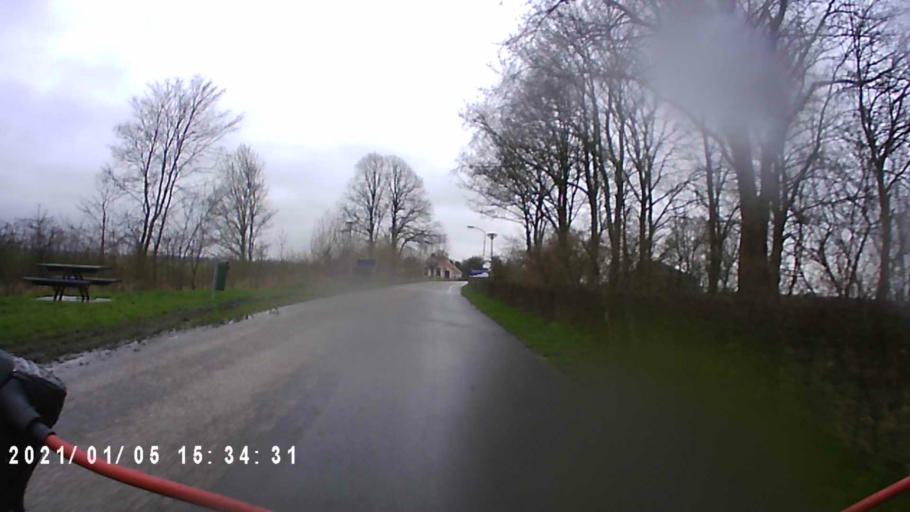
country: DE
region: Lower Saxony
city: Bunde
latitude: 53.2115
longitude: 7.1744
